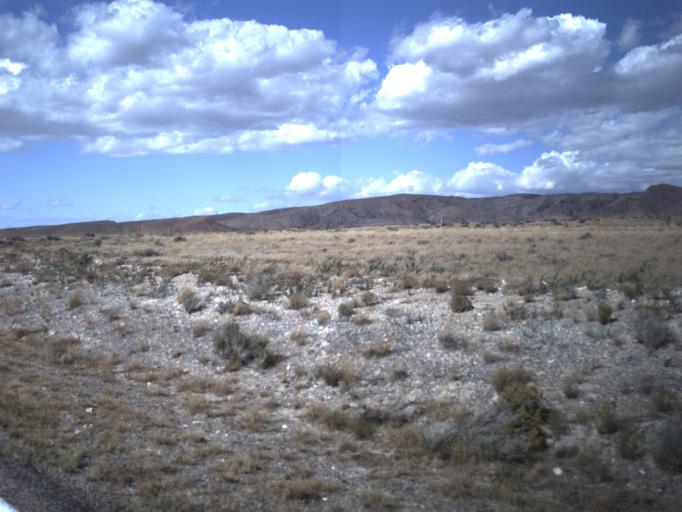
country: US
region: Utah
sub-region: Beaver County
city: Milford
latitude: 38.7875
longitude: -112.9164
